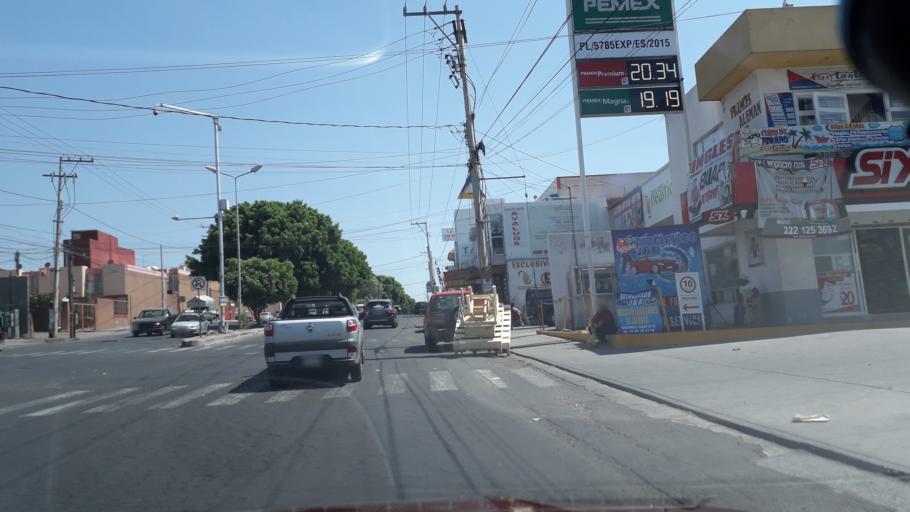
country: MX
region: Puebla
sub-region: Puebla
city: El Capulo (La Quebradora)
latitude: 18.9741
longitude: -98.2188
